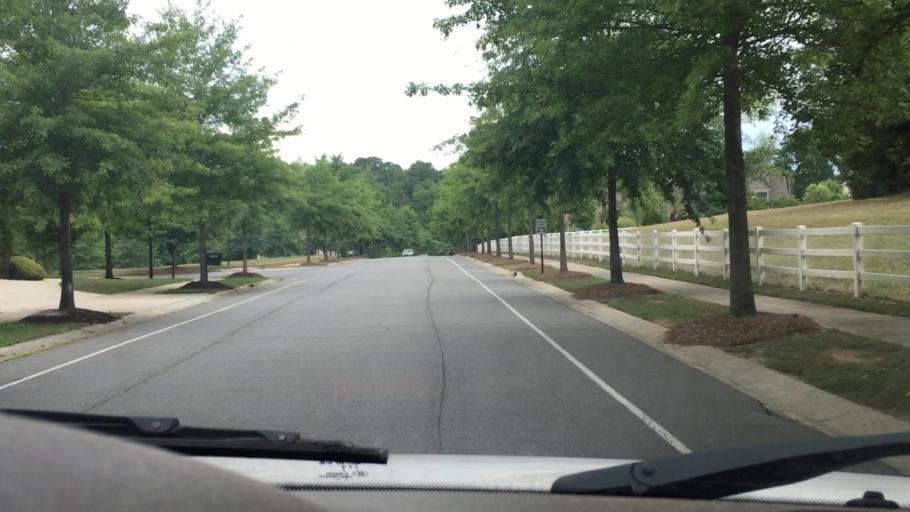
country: US
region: North Carolina
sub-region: Gaston County
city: Davidson
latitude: 35.4635
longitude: -80.7796
